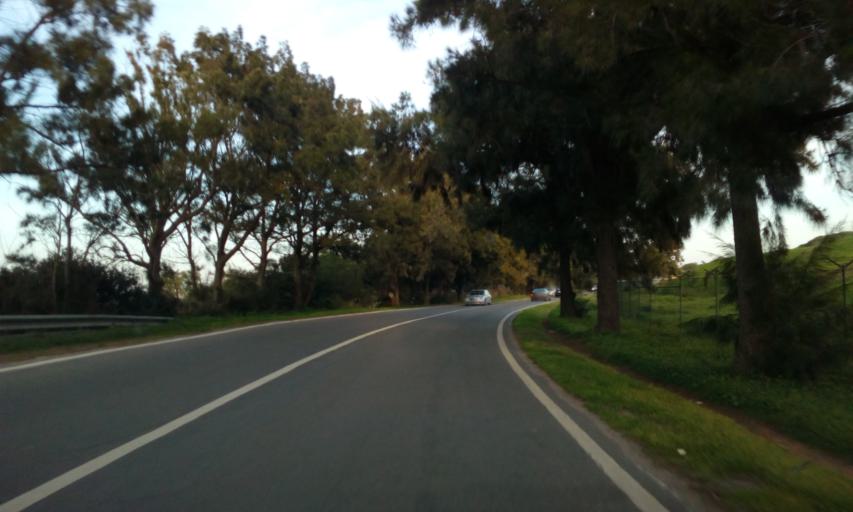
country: PT
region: Faro
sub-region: Faro
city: Faro
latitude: 37.0195
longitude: -7.9866
